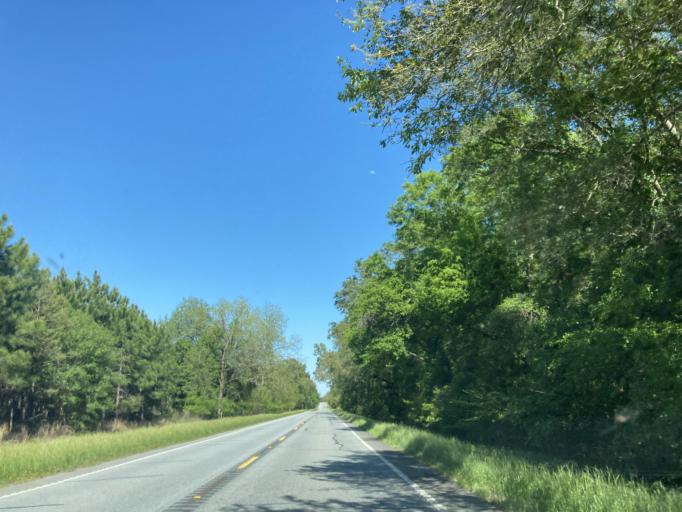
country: US
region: Georgia
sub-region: Miller County
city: Colquitt
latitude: 31.1861
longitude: -84.5315
